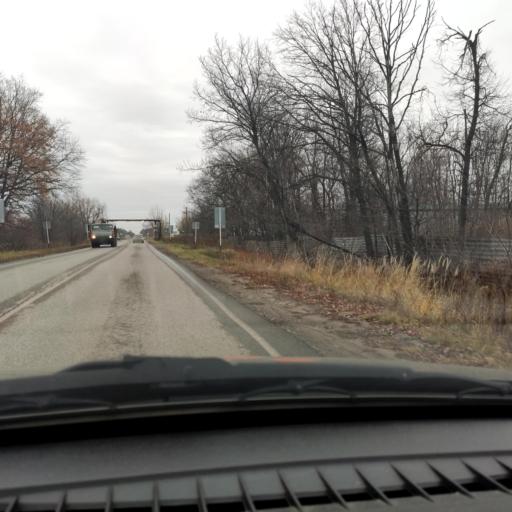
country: RU
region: Samara
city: Zhigulevsk
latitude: 53.3406
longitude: 49.4669
